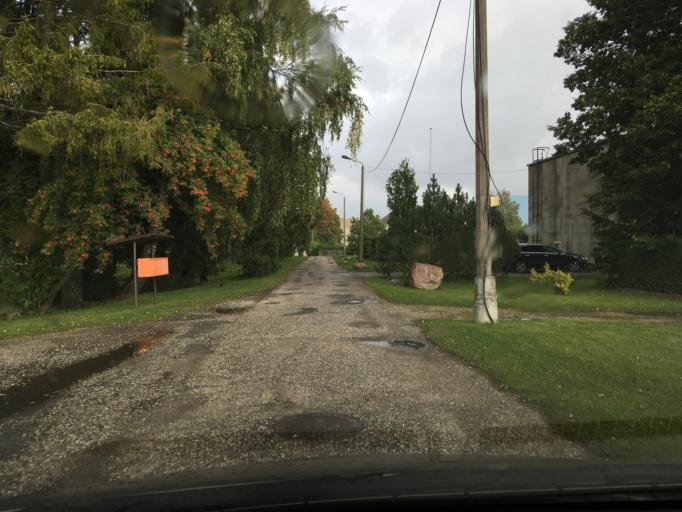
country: EE
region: Raplamaa
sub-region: Rapla vald
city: Rapla
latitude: 58.9904
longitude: 24.8298
